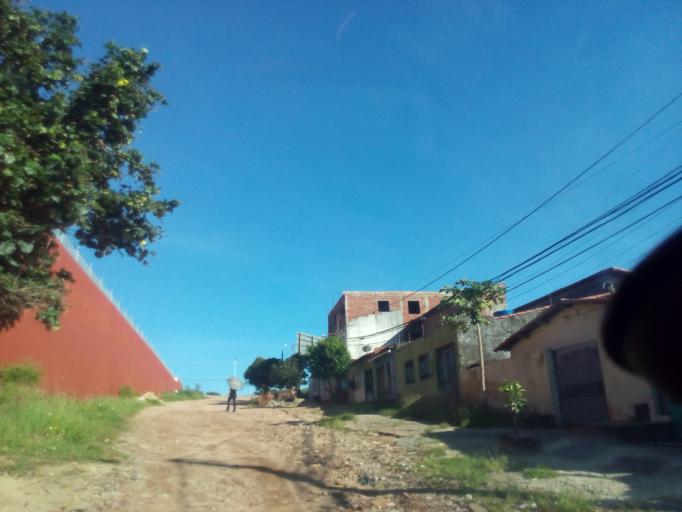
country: BR
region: Rio Grande do Norte
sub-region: Parnamirim
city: Parnamirim
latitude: -5.8652
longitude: -35.2148
